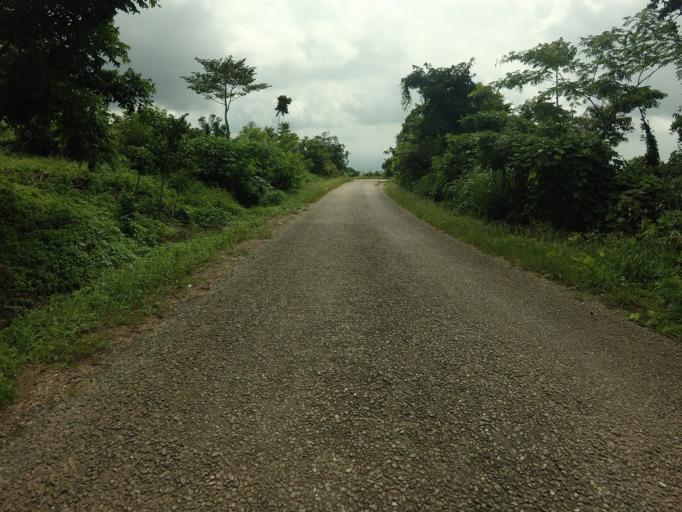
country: GH
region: Volta
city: Kpandu
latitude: 6.8445
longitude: 0.4328
